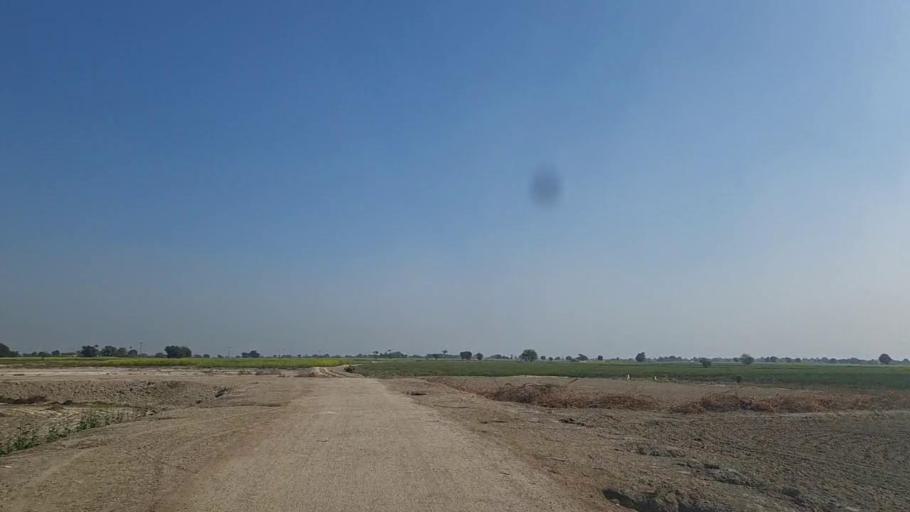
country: PK
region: Sindh
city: Shahpur Chakar
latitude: 26.1958
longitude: 68.5950
